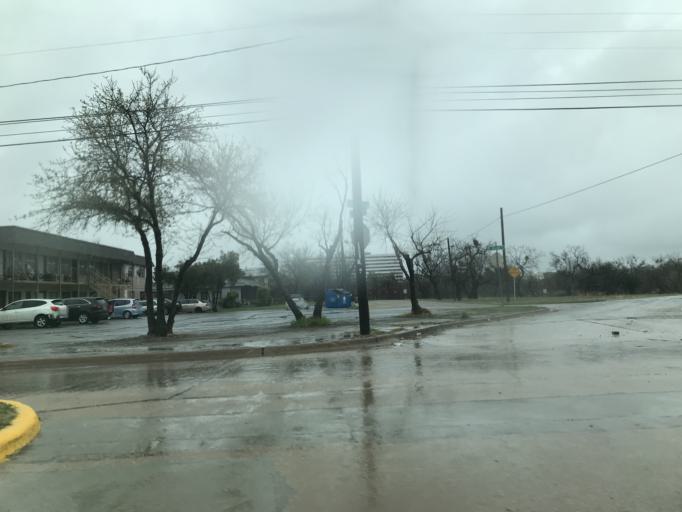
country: US
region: Texas
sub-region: Tom Green County
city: San Angelo
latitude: 31.4654
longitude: -100.4283
